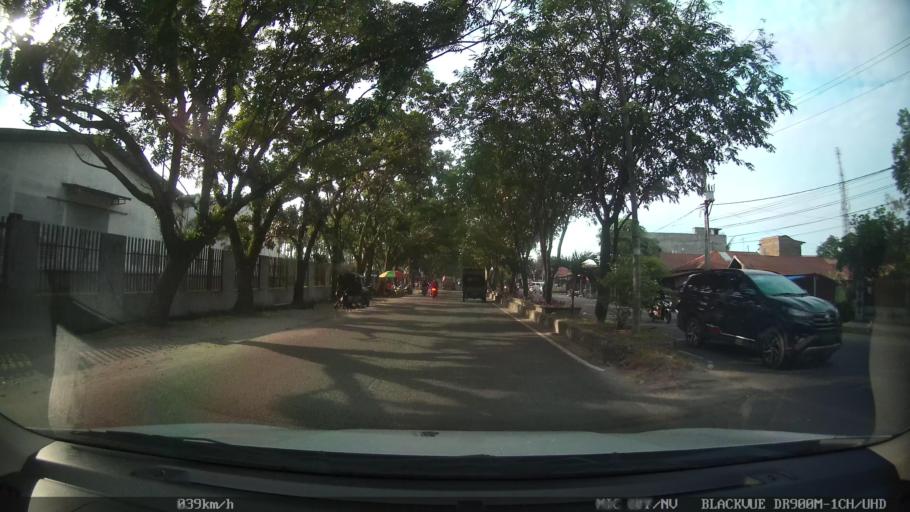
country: ID
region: North Sumatra
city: Sunggal
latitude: 3.5602
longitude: 98.6169
